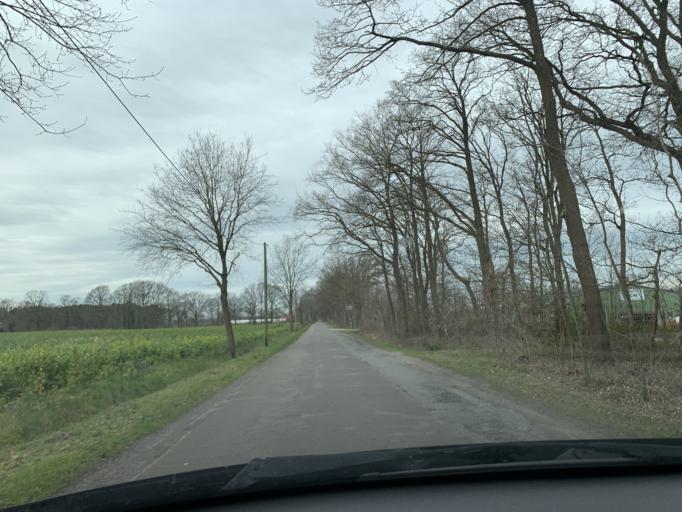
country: DE
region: Lower Saxony
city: Bad Zwischenahn
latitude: 53.2046
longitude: 7.9653
